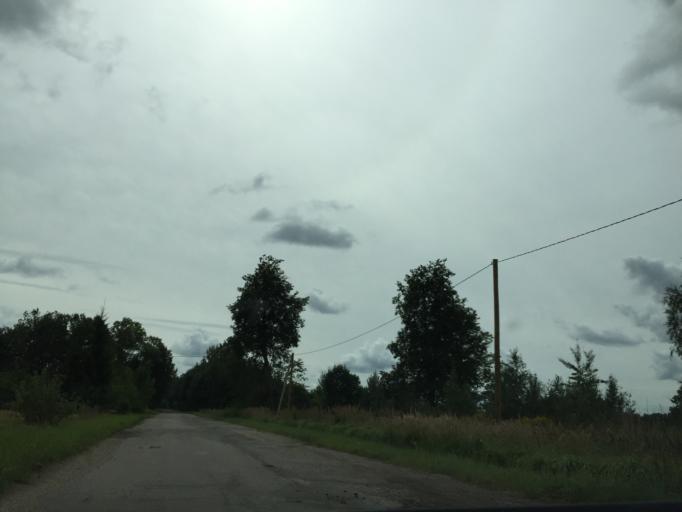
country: LV
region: Lielvarde
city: Lielvarde
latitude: 56.7566
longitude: 24.8419
